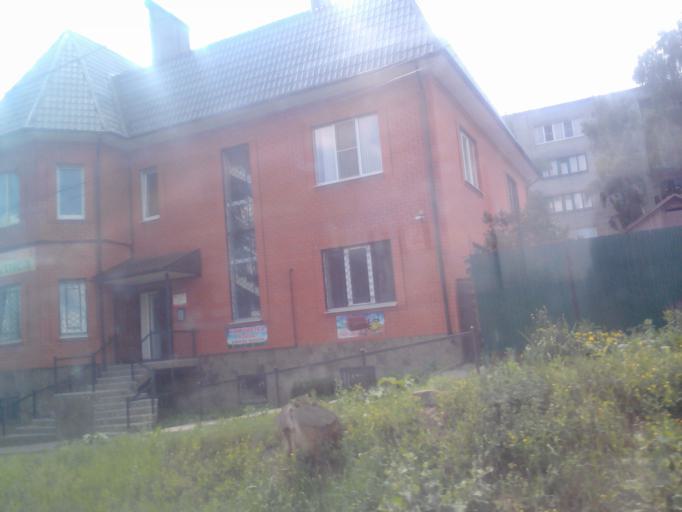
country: RU
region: Kursk
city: Kursk
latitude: 51.7359
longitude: 36.1766
